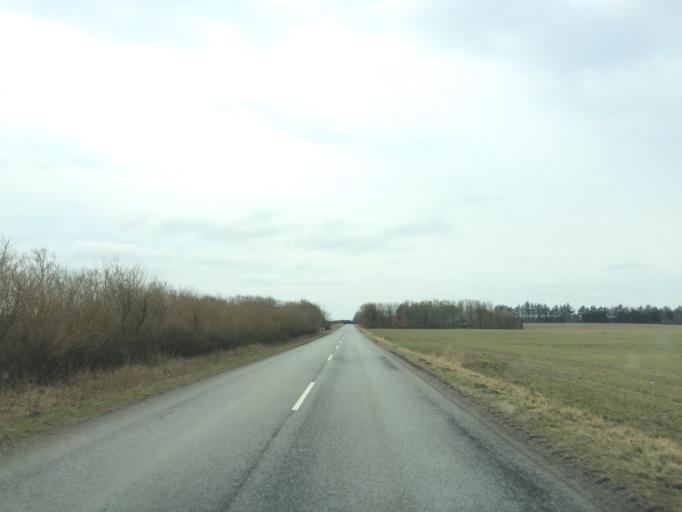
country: DK
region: Central Jutland
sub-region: Ringkobing-Skjern Kommune
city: Tarm
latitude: 55.8390
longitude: 8.4655
